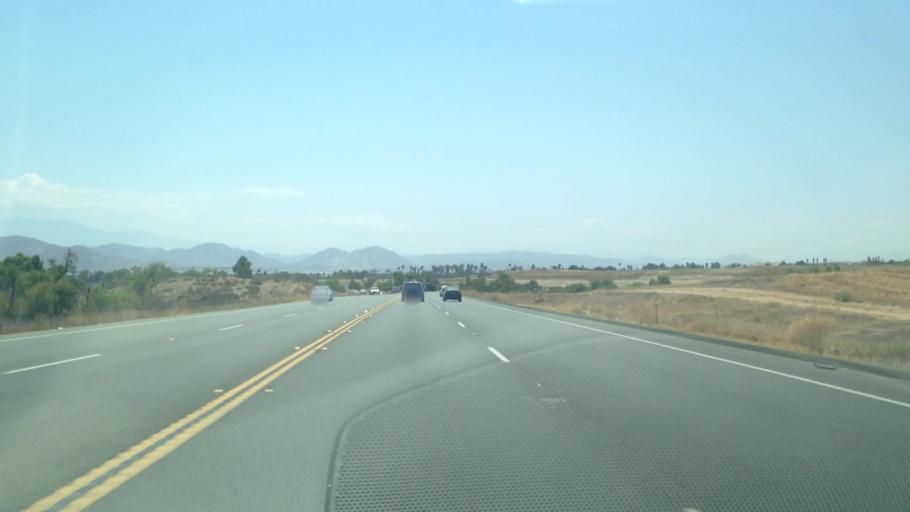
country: US
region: California
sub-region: Riverside County
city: March Air Force Base
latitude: 33.8865
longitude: -117.2986
